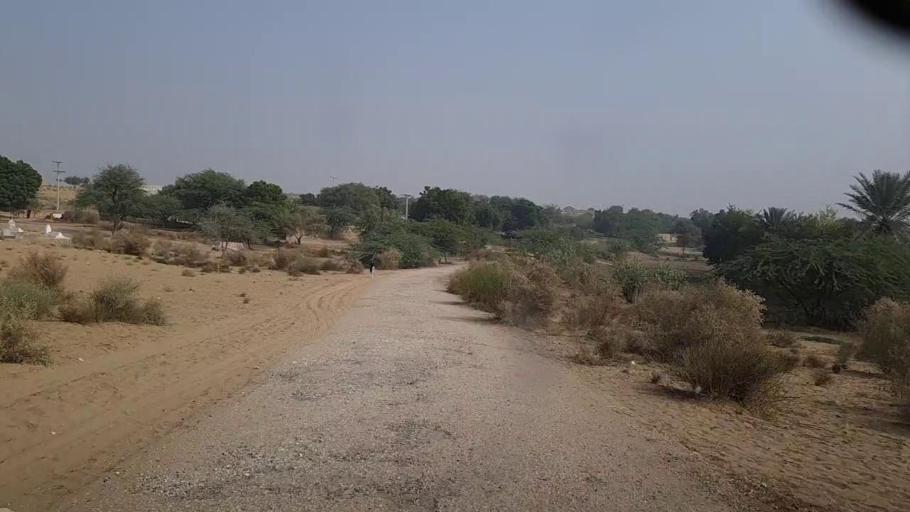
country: PK
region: Sindh
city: Bozdar
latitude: 27.0594
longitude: 68.6503
